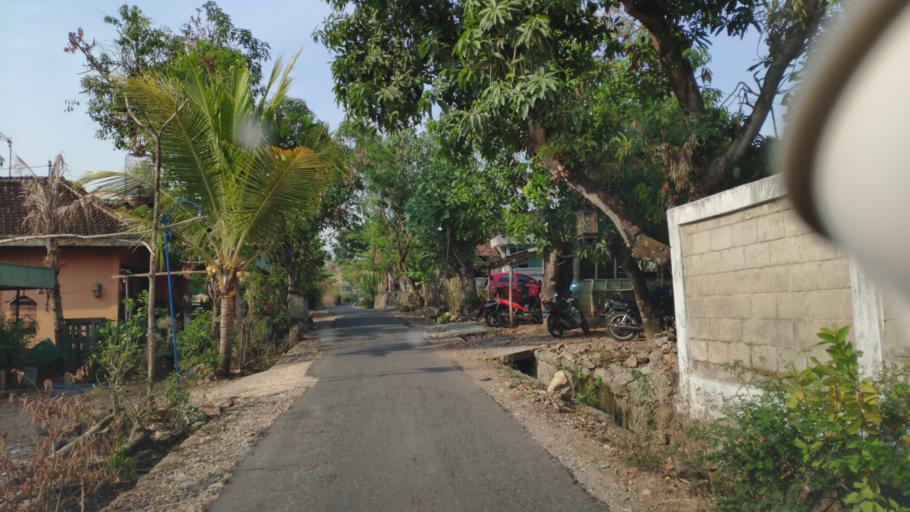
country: ID
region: Central Java
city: Tegalgunung
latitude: -6.9581
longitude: 111.4182
